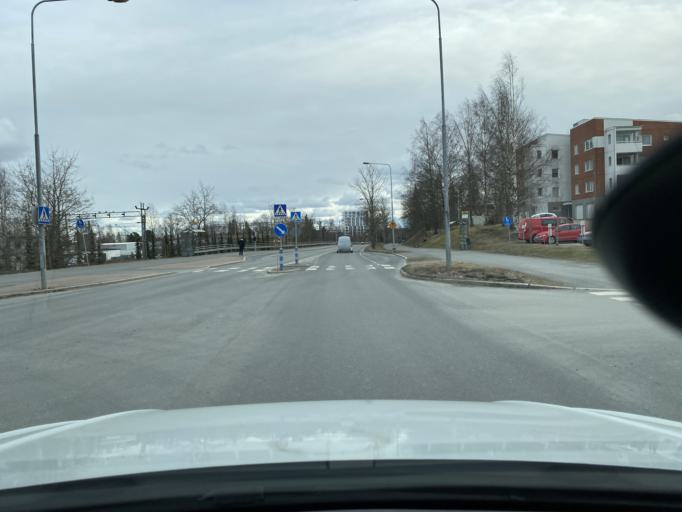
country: FI
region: Pirkanmaa
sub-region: Tampere
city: Lempaeaelae
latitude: 61.3115
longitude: 23.7531
